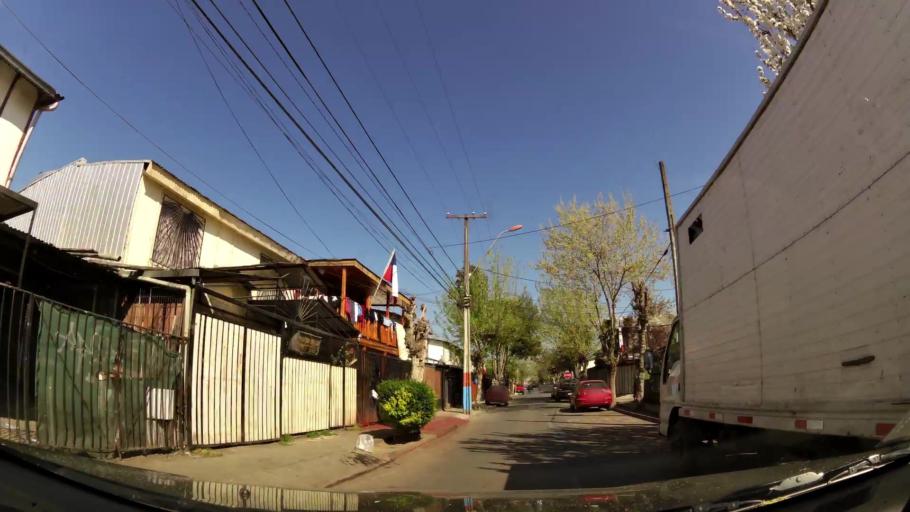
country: CL
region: Santiago Metropolitan
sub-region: Provincia de Chacabuco
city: Chicureo Abajo
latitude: -33.3560
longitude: -70.6887
